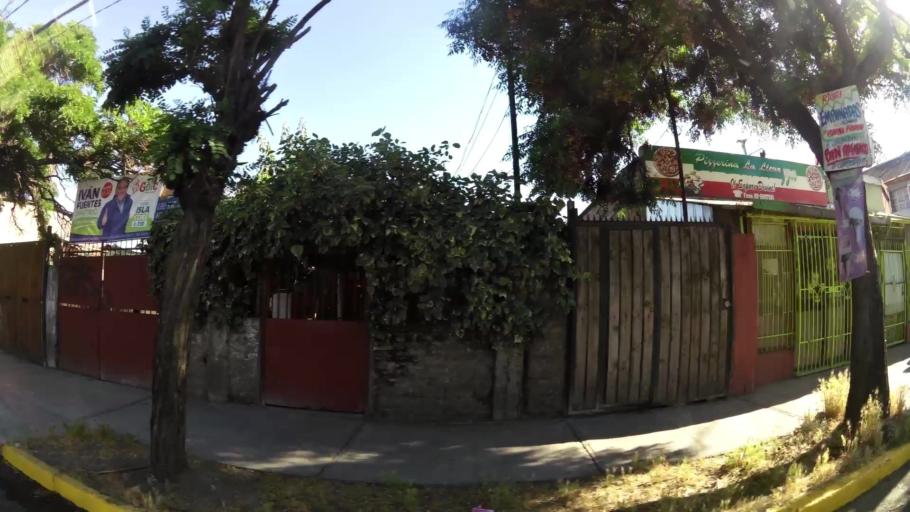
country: CL
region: Santiago Metropolitan
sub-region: Provincia de Maipo
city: San Bernardo
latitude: -33.5496
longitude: -70.6806
